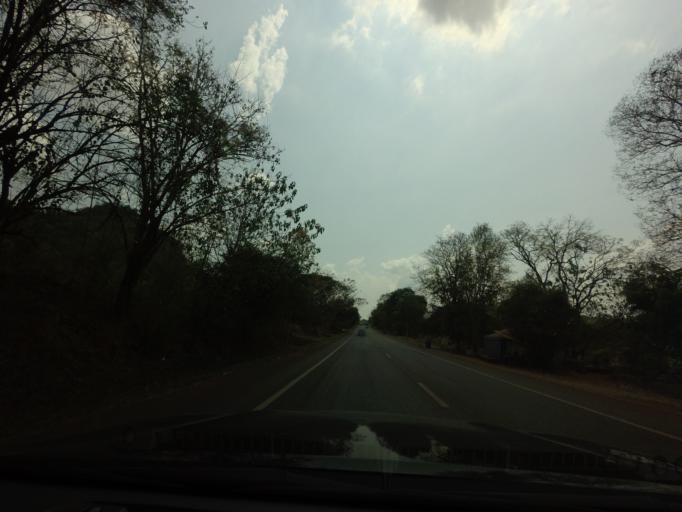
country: TH
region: Kanchanaburi
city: Sai Yok
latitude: 14.1455
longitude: 99.1456
